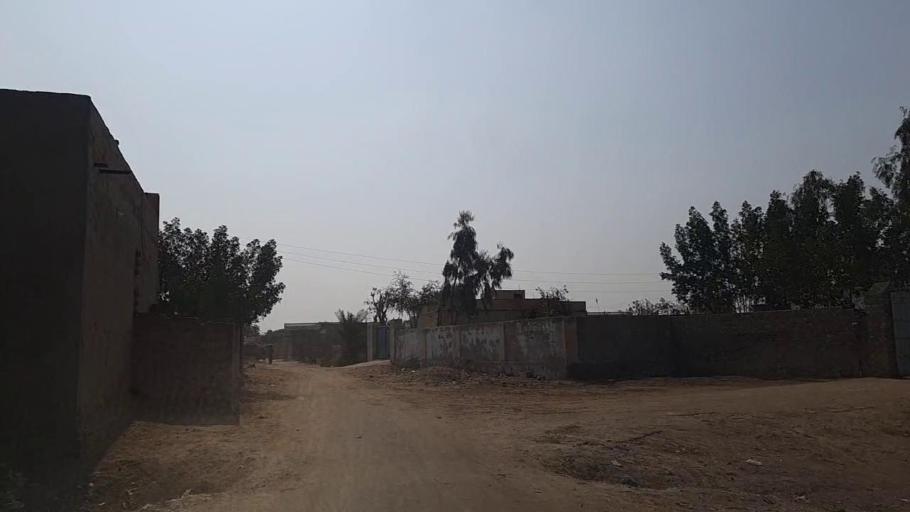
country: PK
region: Sindh
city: Daur
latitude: 26.4481
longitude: 68.4427
